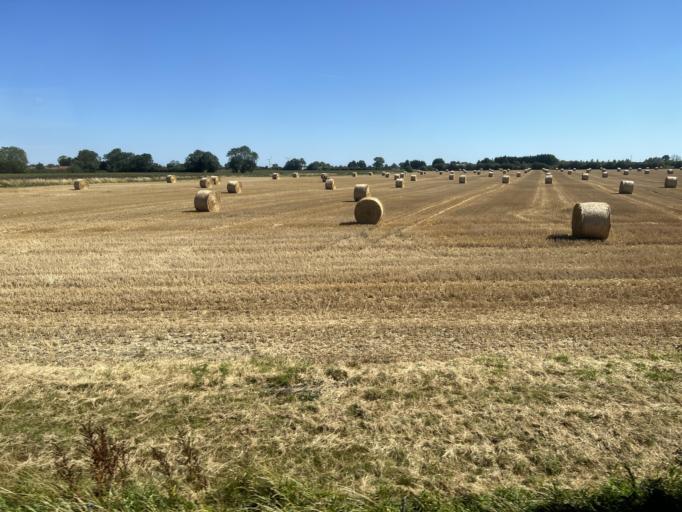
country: GB
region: England
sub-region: Lincolnshire
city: Wainfleet All Saints
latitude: 53.1294
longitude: 0.1942
